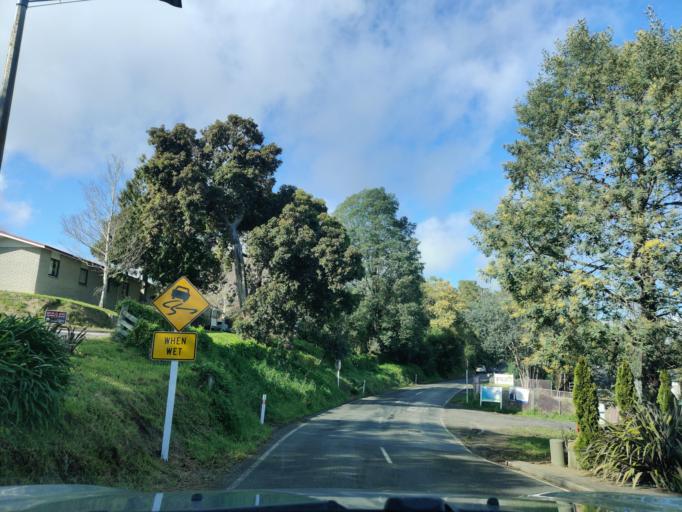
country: NZ
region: Hawke's Bay
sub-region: Hastings District
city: Hastings
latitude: -39.6760
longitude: 176.8958
